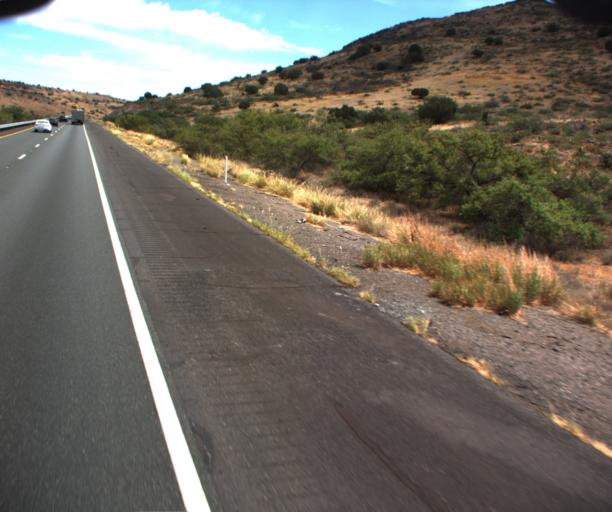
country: US
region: Arizona
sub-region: Yavapai County
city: Cordes Lakes
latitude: 34.4733
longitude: -112.0221
